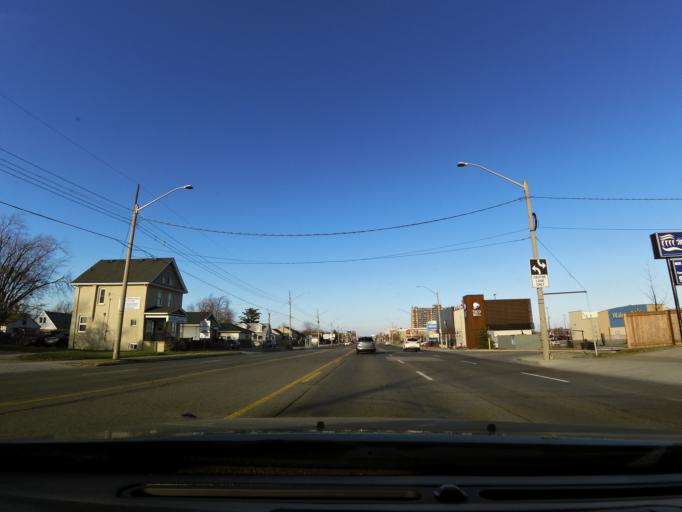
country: CA
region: Ontario
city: Hamilton
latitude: 43.2339
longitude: -79.8793
